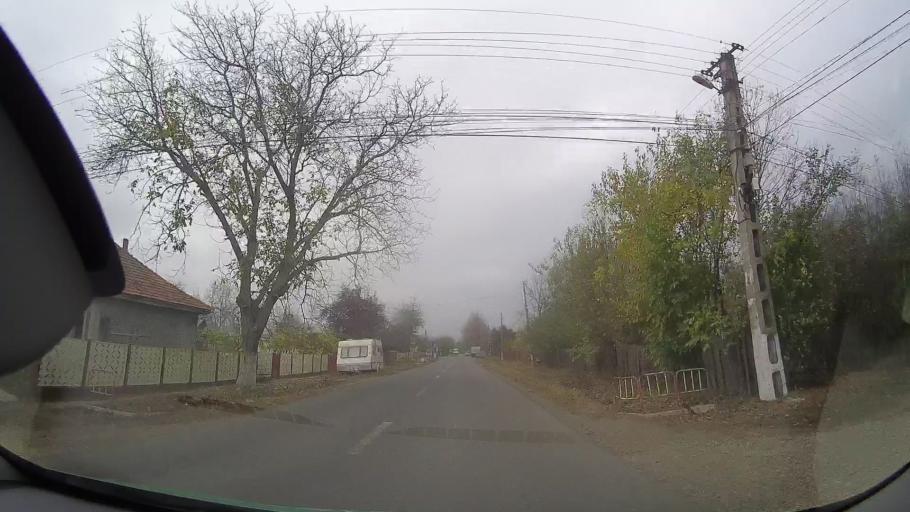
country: RO
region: Buzau
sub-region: Comuna Scutelnici
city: Scutelnici
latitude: 44.8779
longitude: 26.8794
